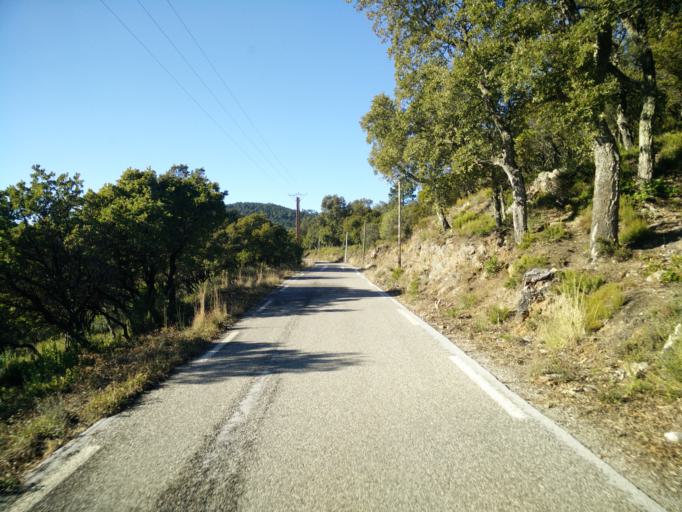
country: FR
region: Provence-Alpes-Cote d'Azur
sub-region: Departement du Var
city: La Garde-Freinet
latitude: 43.2560
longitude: 6.4198
